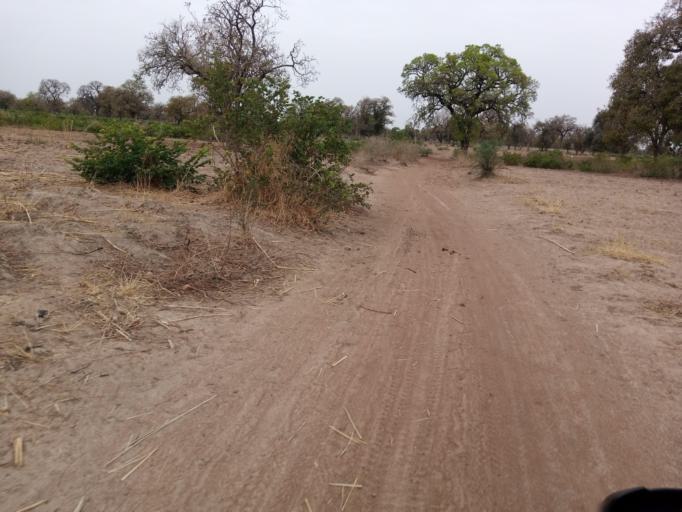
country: BF
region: Boucle du Mouhoun
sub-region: Province de la Kossi
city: Nouna
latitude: 12.7689
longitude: -4.0599
